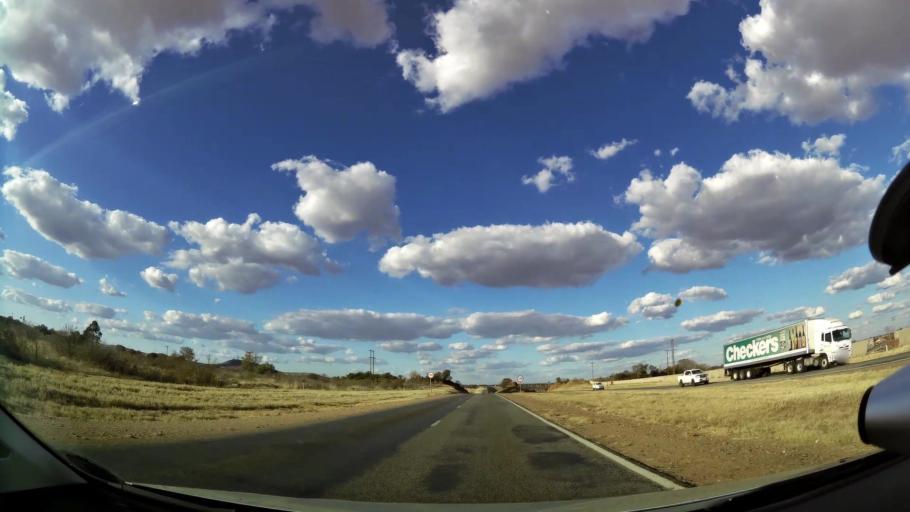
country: ZA
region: North-West
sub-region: Dr Kenneth Kaunda District Municipality
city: Stilfontein
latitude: -26.7891
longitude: 26.9234
